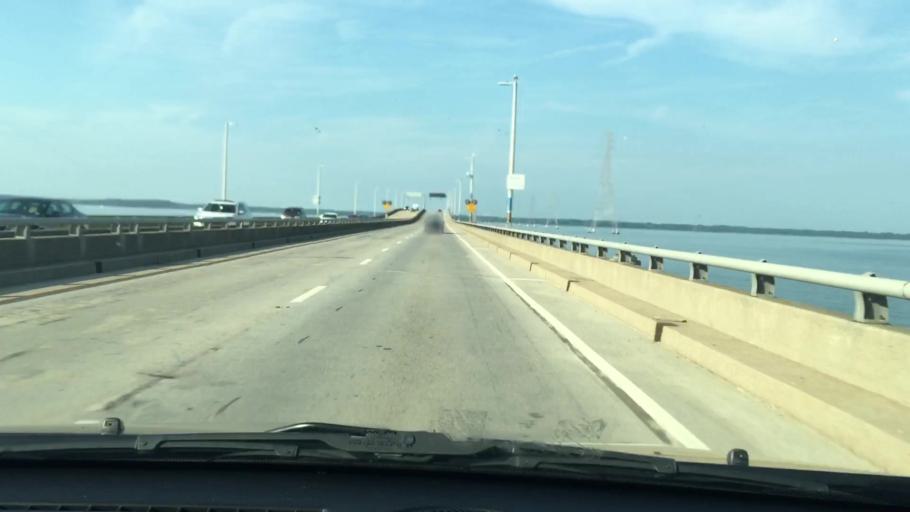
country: US
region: Virginia
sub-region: City of Newport News
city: Newport News
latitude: 36.9977
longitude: -76.4752
